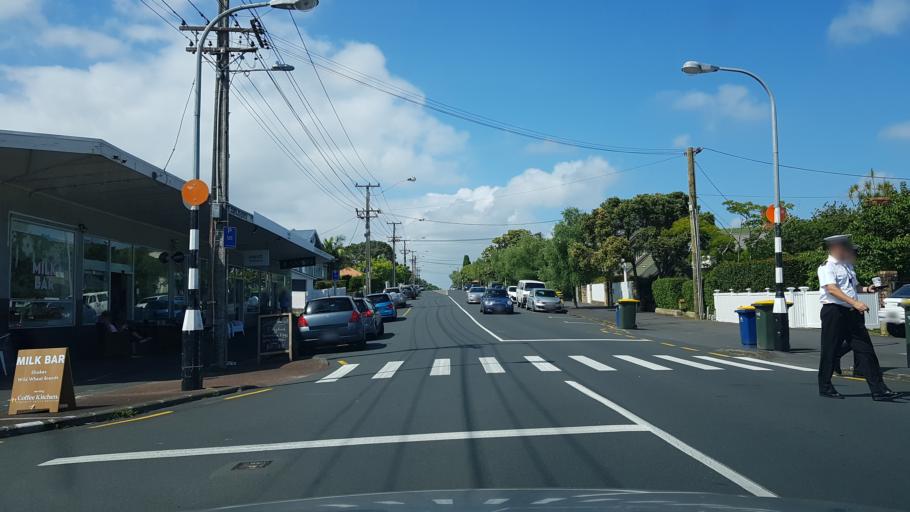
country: NZ
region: Auckland
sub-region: Auckland
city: North Shore
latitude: -36.8210
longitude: 174.8050
